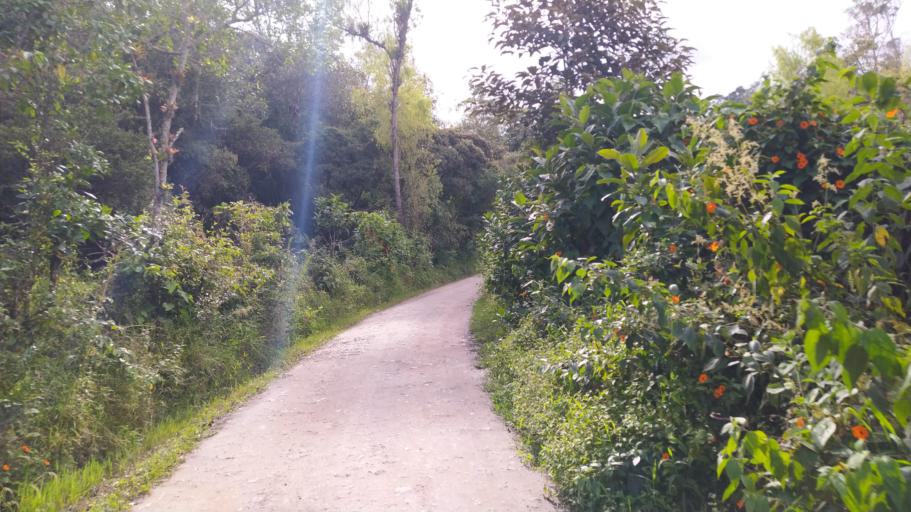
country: CO
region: Cundinamarca
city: Tenza
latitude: 5.0922
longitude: -73.4582
